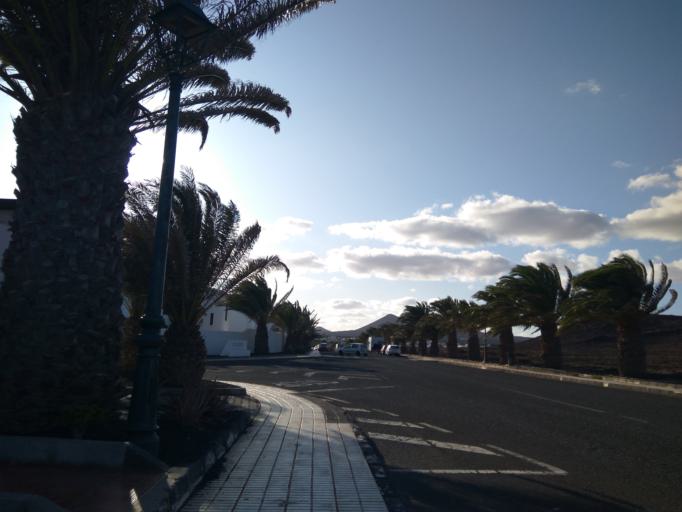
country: ES
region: Canary Islands
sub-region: Provincia de Las Palmas
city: Arrecife
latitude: 29.0072
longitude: -13.4902
